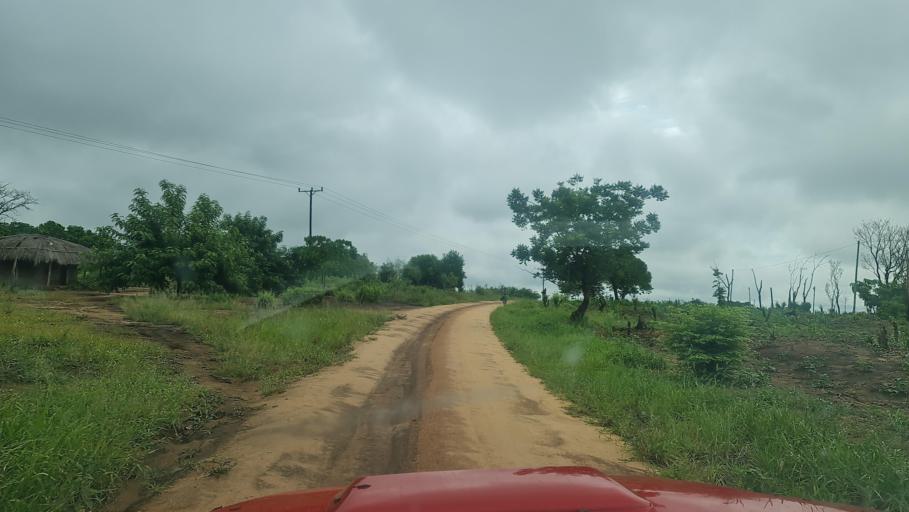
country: MW
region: Southern Region
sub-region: Nsanje District
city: Nsanje
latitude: -17.1780
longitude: 35.9007
